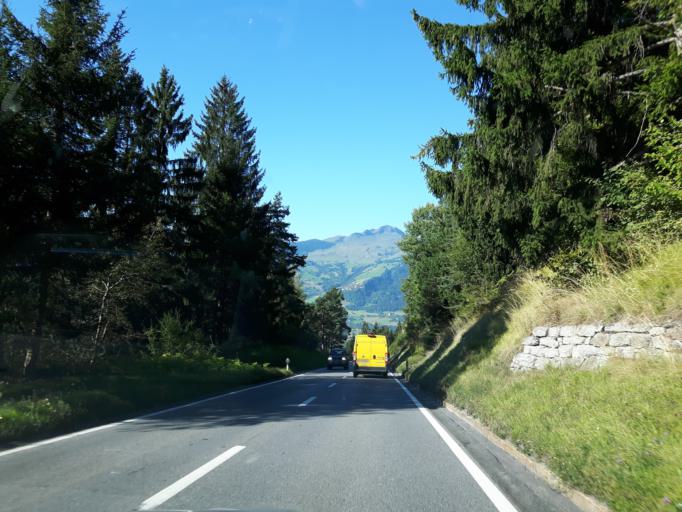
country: CH
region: Grisons
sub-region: Surselva District
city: Laax
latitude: 46.7919
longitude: 9.2437
